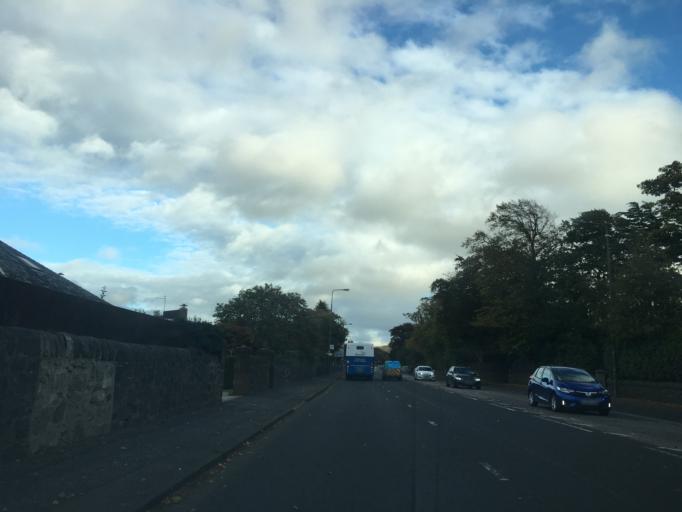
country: GB
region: Scotland
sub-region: Edinburgh
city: Currie
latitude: 55.9612
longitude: -3.3104
